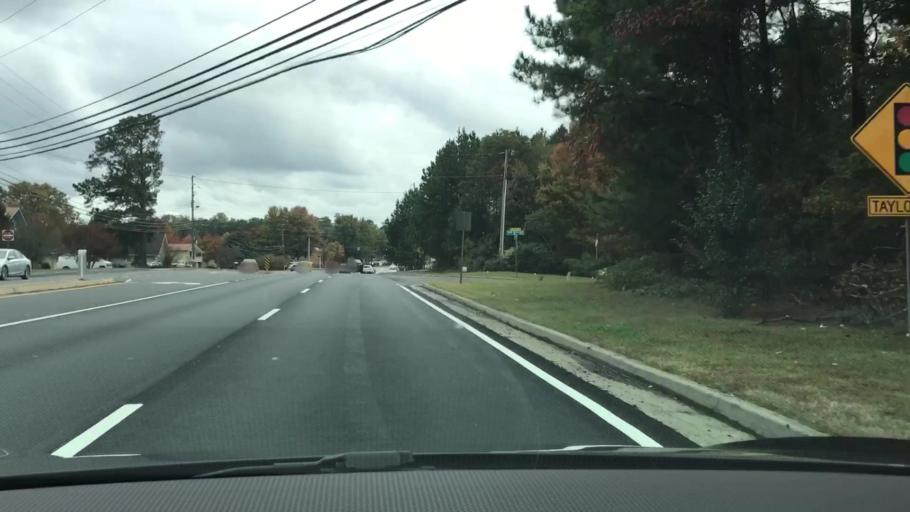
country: US
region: Georgia
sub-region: Gwinnett County
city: Suwanee
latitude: 34.0063
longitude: -84.0417
